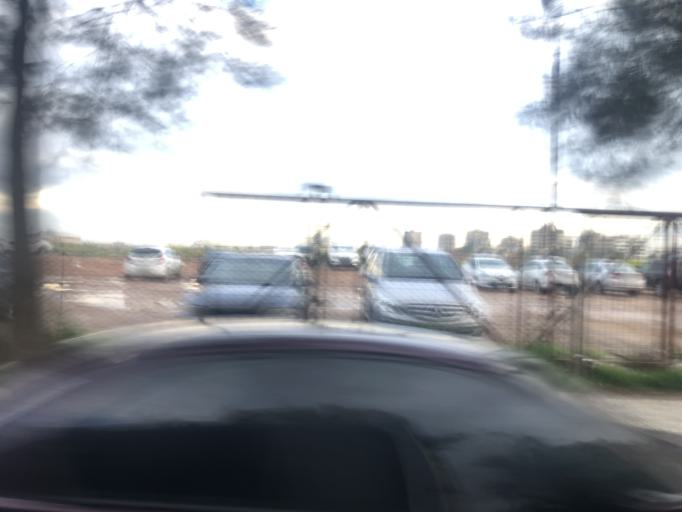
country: TR
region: Izmir
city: Karsiyaka
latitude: 38.4707
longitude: 27.0669
